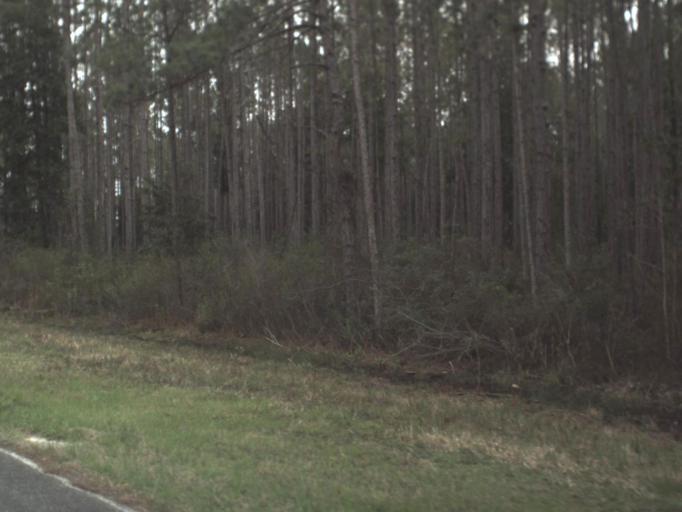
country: US
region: Florida
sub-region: Gadsden County
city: Midway
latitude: 30.3759
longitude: -84.5568
